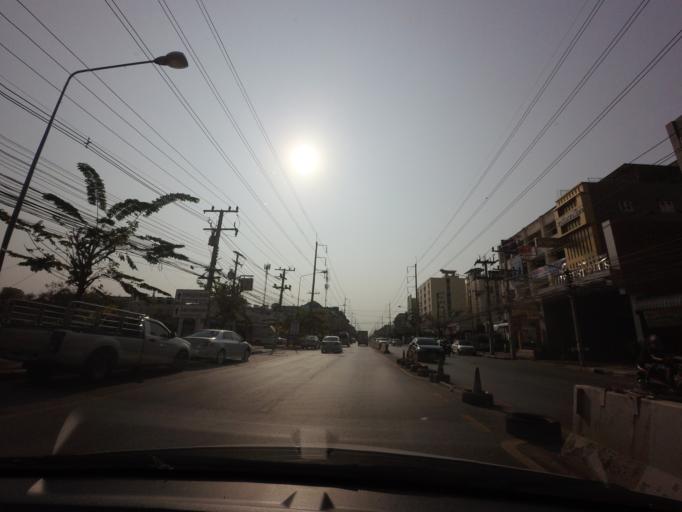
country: TH
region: Nakhon Pathom
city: Salaya
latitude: 13.8013
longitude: 100.3160
